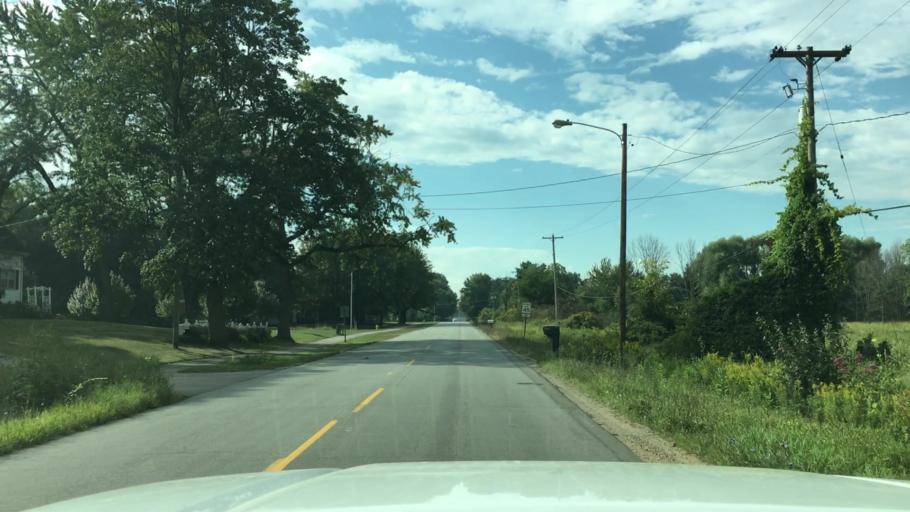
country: US
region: Michigan
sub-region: Ottawa County
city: Hudsonville
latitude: 42.8222
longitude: -85.8422
